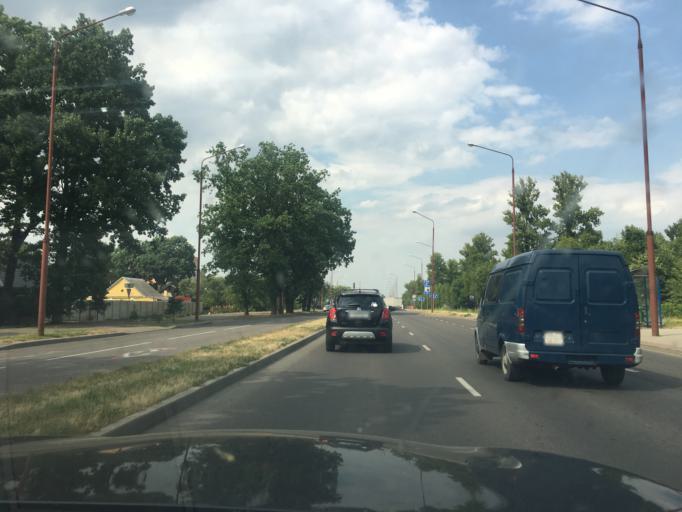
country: BY
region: Brest
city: Brest
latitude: 52.1331
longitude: 23.6748
